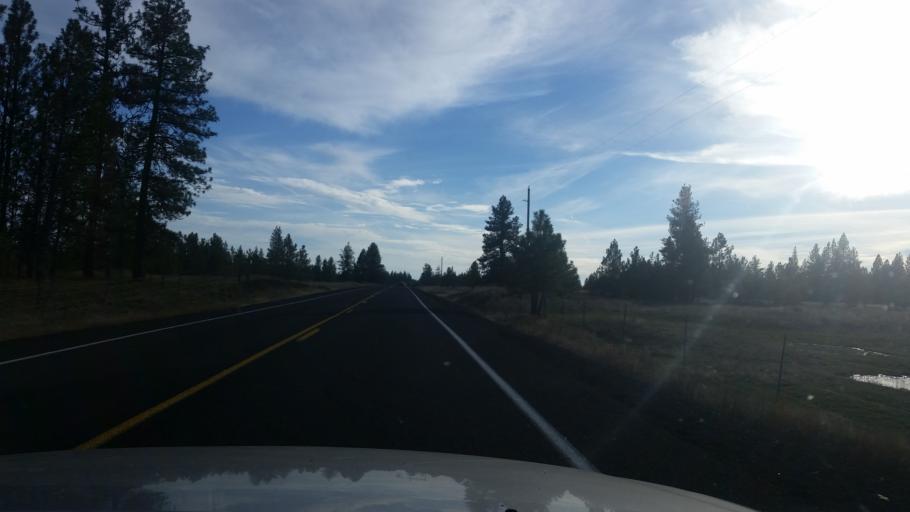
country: US
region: Washington
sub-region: Spokane County
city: Cheney
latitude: 47.3800
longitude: -117.5849
